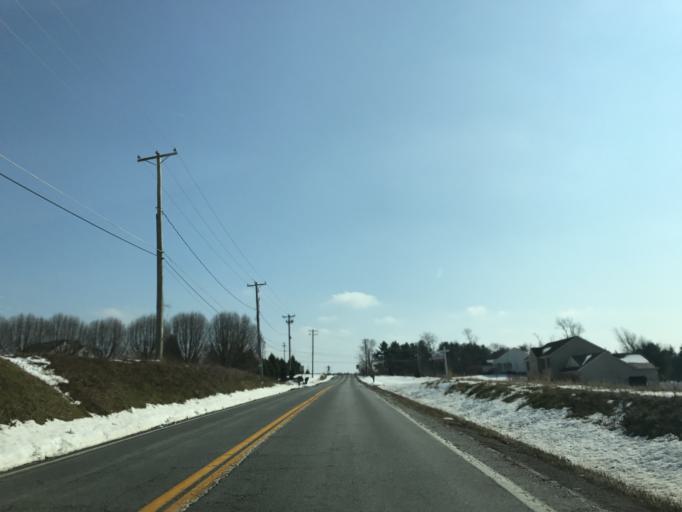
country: US
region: Pennsylvania
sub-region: York County
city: Susquehanna Trails
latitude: 39.6822
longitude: -76.3890
